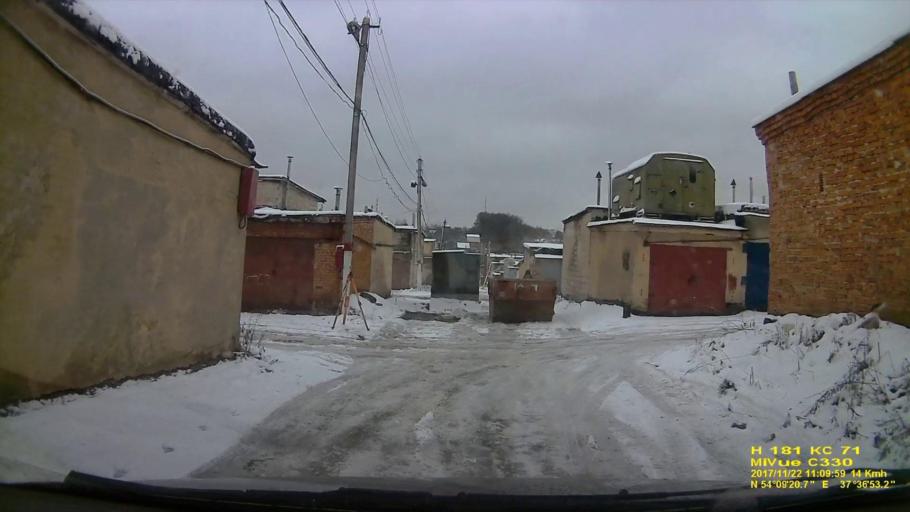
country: RU
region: Tula
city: Mendeleyevskiy
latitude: 54.1557
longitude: 37.6147
